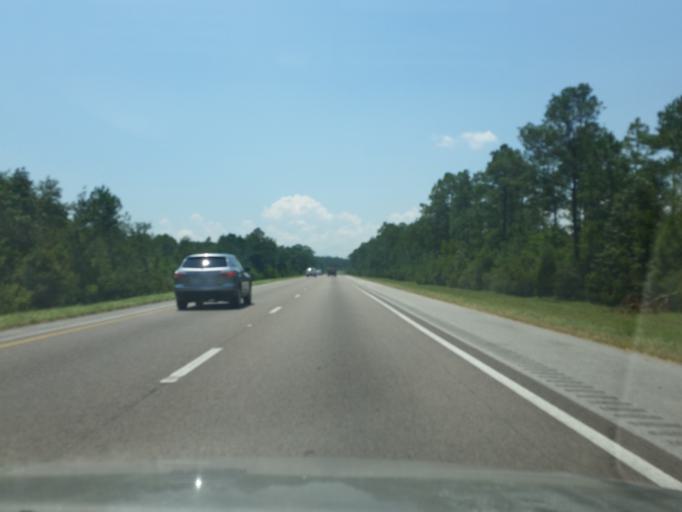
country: US
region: Florida
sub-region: Escambia County
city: Cantonment
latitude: 30.5781
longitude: -87.4549
